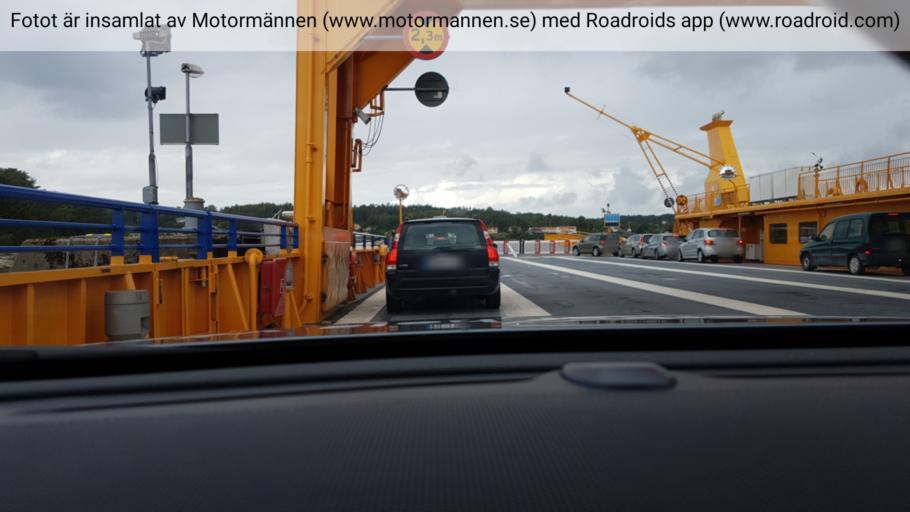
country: SE
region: Vaestra Goetaland
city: Svanesund
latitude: 58.1341
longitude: 11.8430
